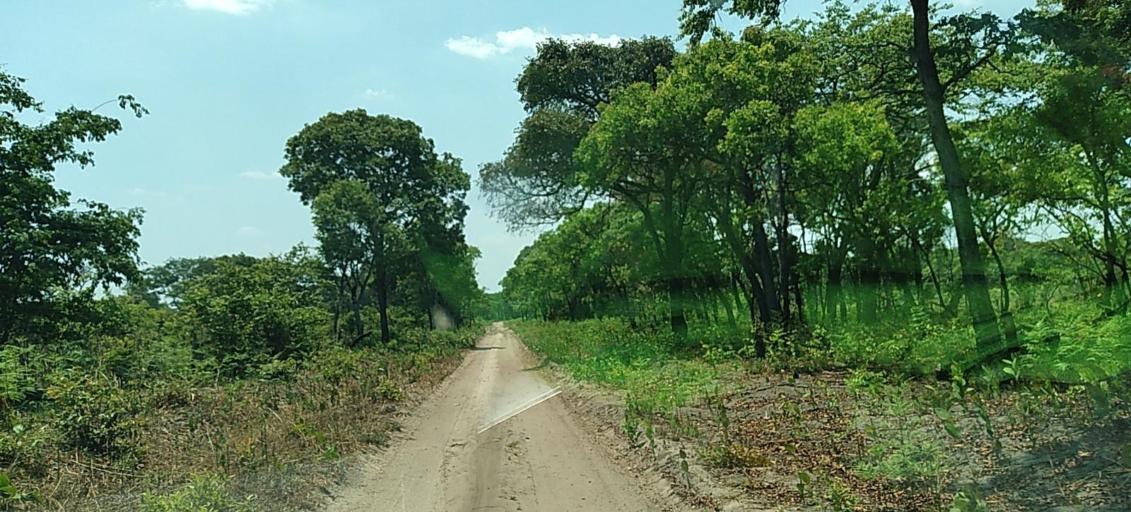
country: CD
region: Katanga
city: Kolwezi
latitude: -11.3083
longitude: 25.2338
